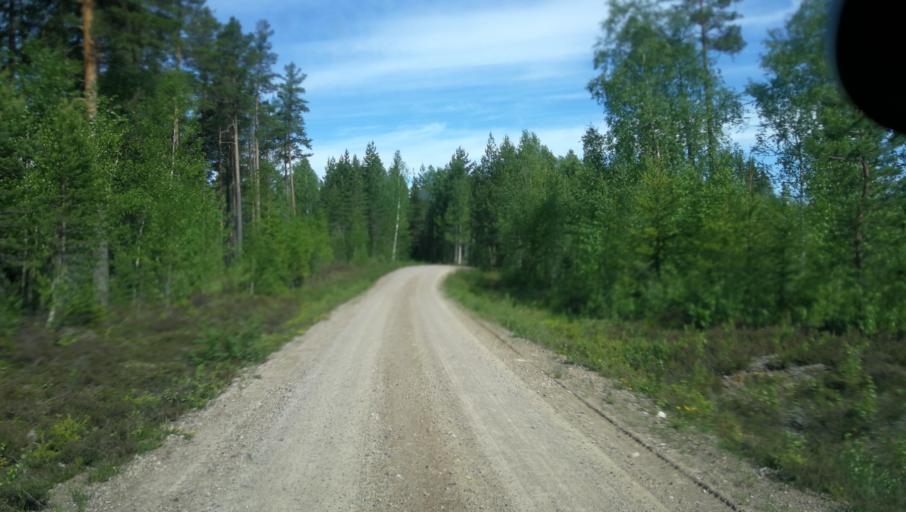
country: SE
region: Dalarna
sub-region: Vansbro Kommun
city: Vansbro
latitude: 60.8235
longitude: 14.1669
